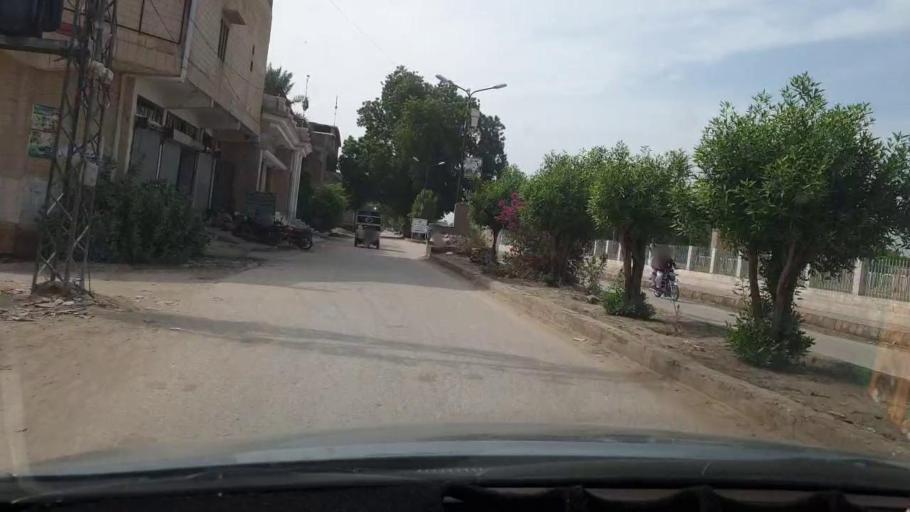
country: PK
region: Sindh
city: Khairpur
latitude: 27.5214
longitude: 68.7570
